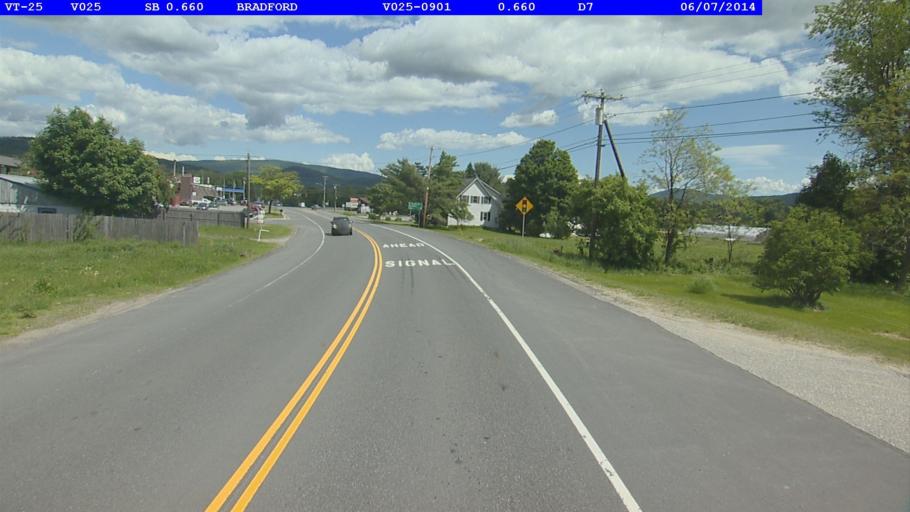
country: US
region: New Hampshire
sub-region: Grafton County
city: Orford
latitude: 43.9821
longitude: -72.1238
